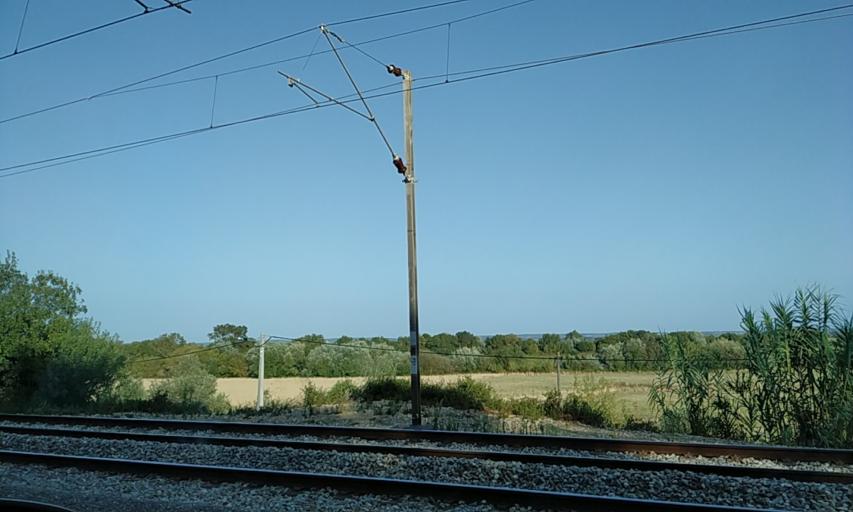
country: PT
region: Santarem
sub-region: Santarem
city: Santarem
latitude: 39.2629
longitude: -8.6653
